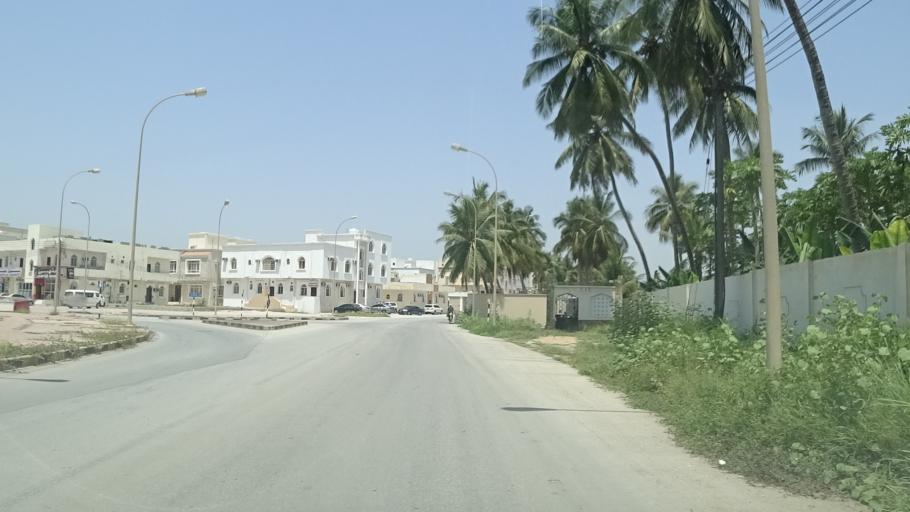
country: OM
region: Zufar
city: Salalah
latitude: 17.0188
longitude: 54.1294
